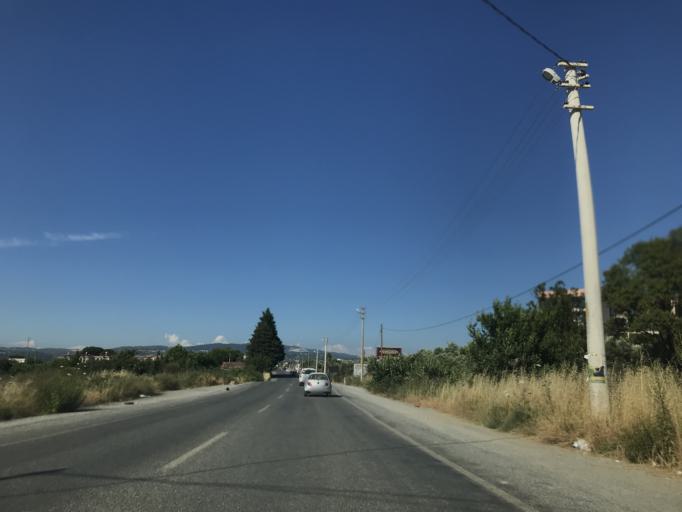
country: TR
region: Aydin
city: Davutlar
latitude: 37.7289
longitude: 27.2677
